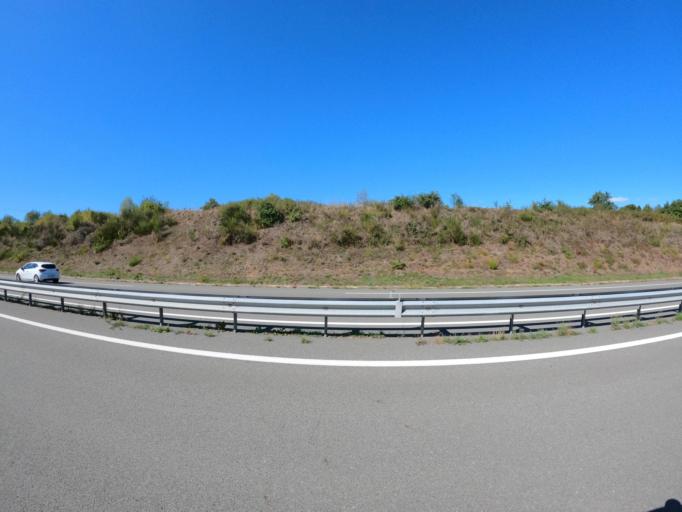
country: FR
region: Limousin
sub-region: Departement de la Creuse
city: Gouzon
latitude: 46.2393
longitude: 2.3298
